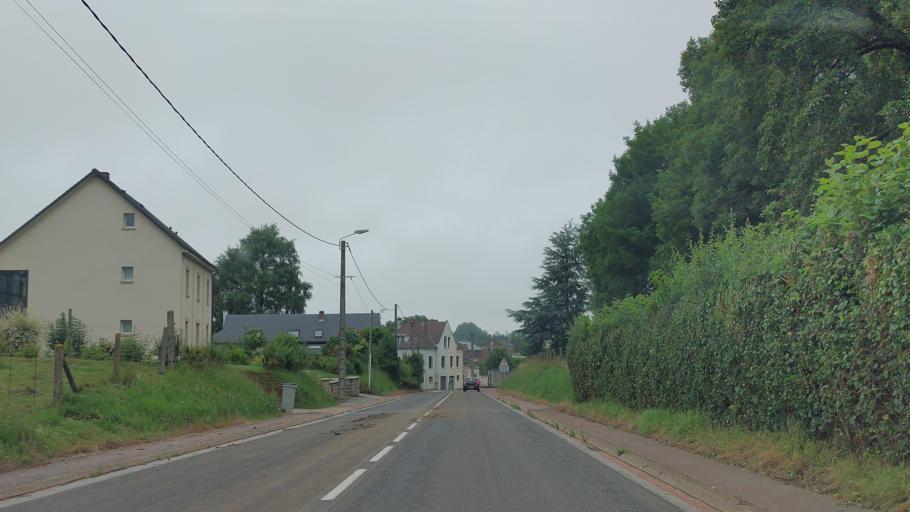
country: FR
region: Picardie
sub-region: Departement de la Somme
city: Bethencourt-sur-Mer
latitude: 50.0751
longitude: 1.5028
